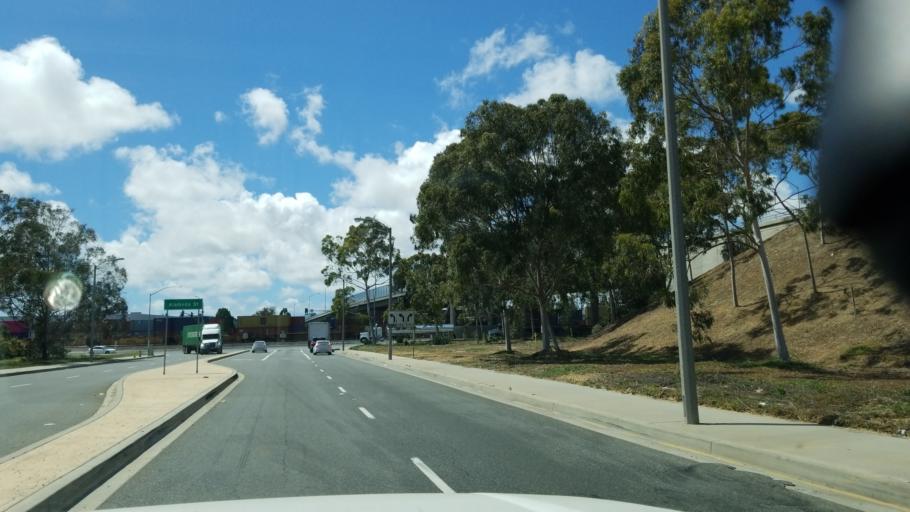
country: US
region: California
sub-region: Los Angeles County
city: Compton
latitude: 33.8461
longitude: -118.2190
